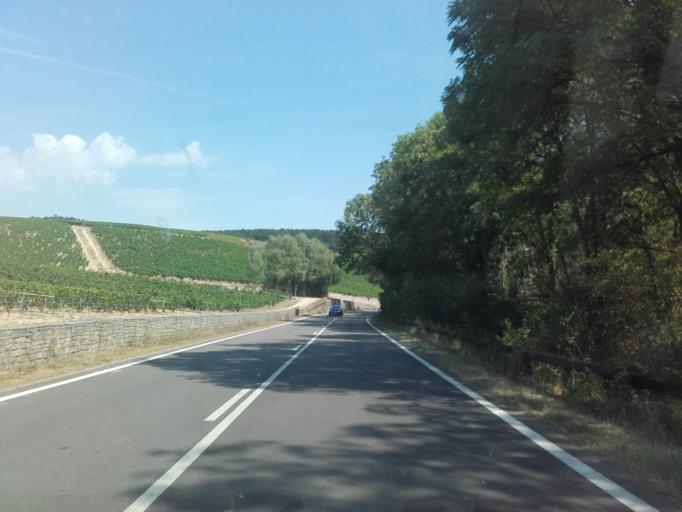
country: FR
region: Bourgogne
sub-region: Departement de l'Yonne
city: Chablis
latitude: 47.8231
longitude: 3.7972
